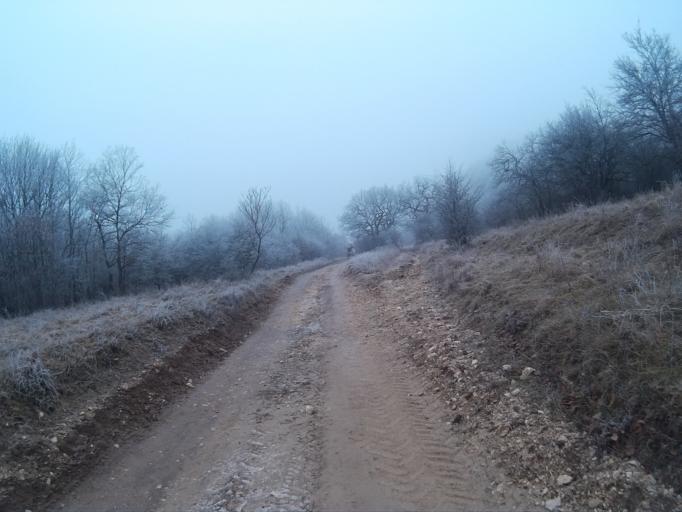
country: HU
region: Fejer
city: Zamoly
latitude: 47.3921
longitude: 18.3641
